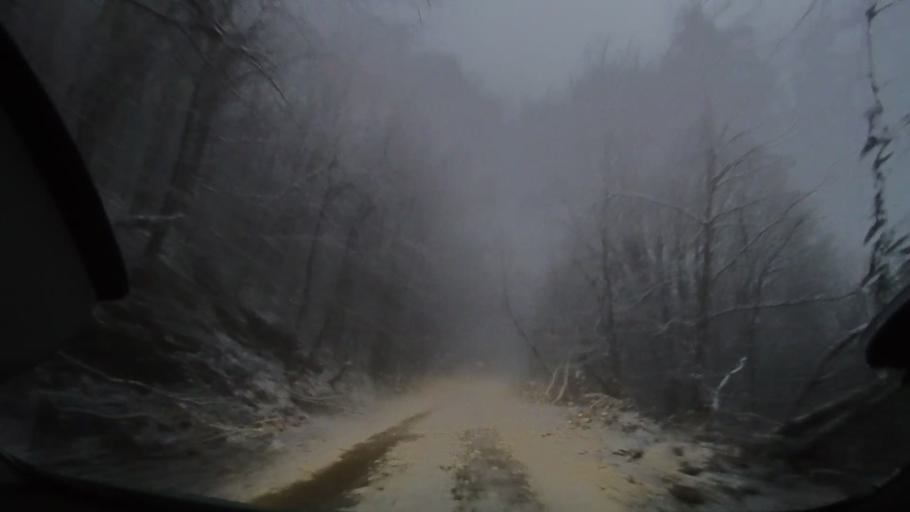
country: RO
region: Alba
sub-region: Comuna Avram Iancu
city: Avram Iancu
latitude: 46.3118
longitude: 22.8080
